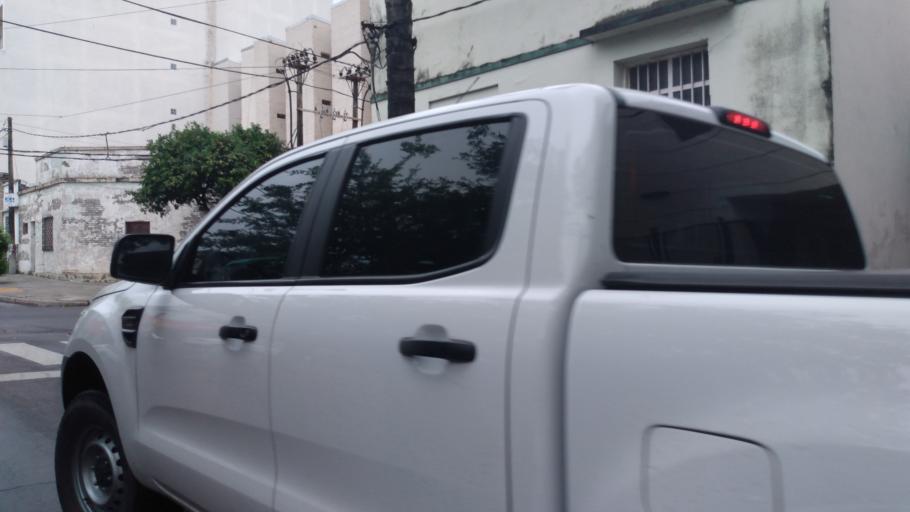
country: AR
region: Corrientes
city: Corrientes
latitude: -27.4637
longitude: -58.8298
